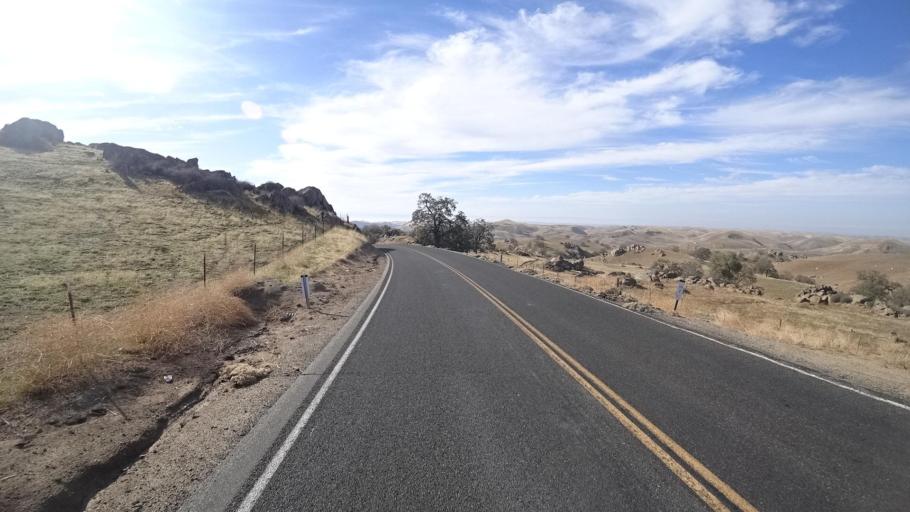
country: US
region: California
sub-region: Kern County
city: Oildale
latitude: 35.6187
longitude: -118.8576
